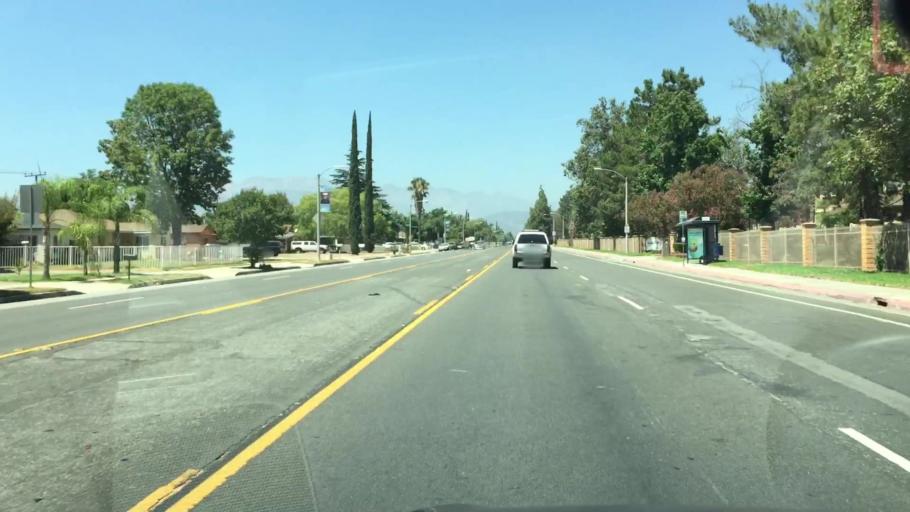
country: US
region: California
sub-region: San Bernardino County
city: Muscoy
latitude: 34.1700
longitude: -117.3176
